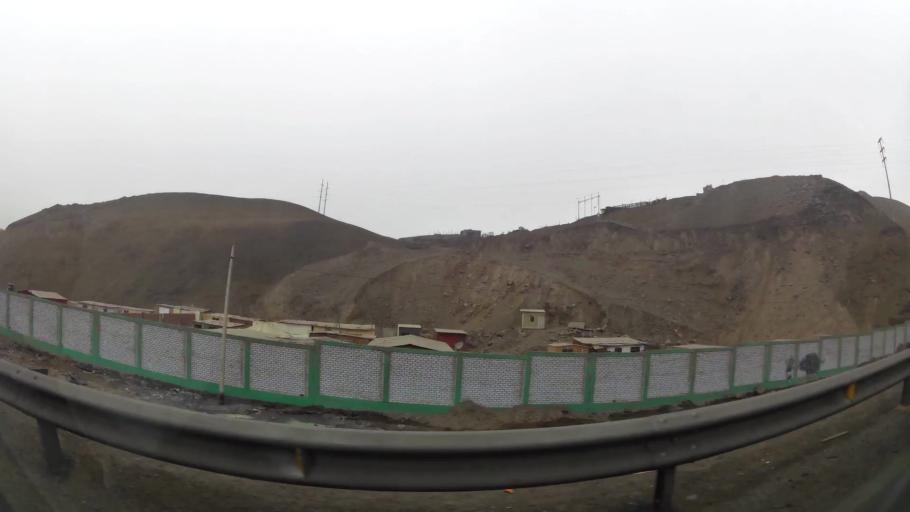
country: PE
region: Lima
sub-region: Lima
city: Santa Rosa
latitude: -11.8198
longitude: -77.1262
